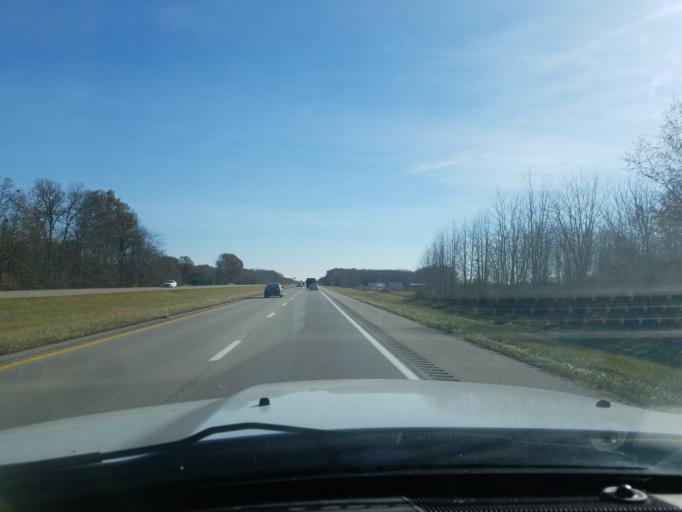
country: US
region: Ohio
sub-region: Brown County
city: Mount Orab
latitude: 39.0528
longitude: -83.9688
